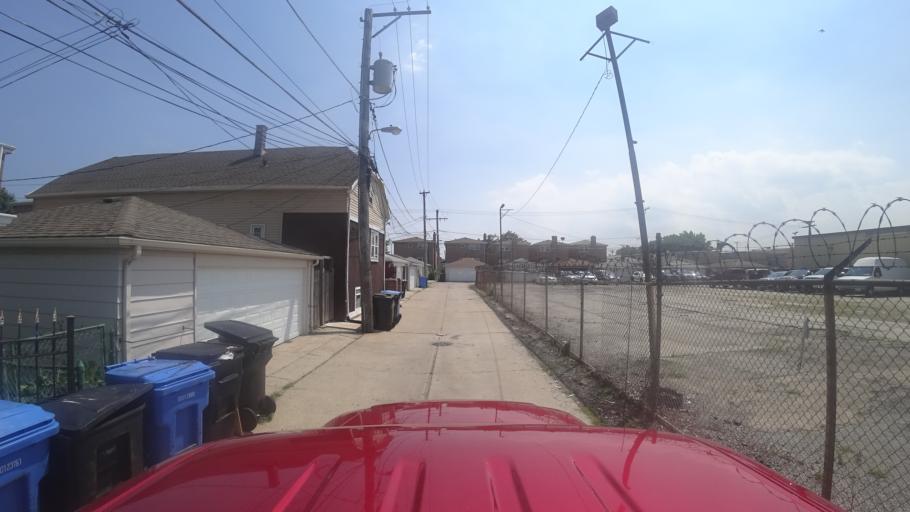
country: US
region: Illinois
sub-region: Cook County
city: Stickney
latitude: 41.7940
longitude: -87.7361
